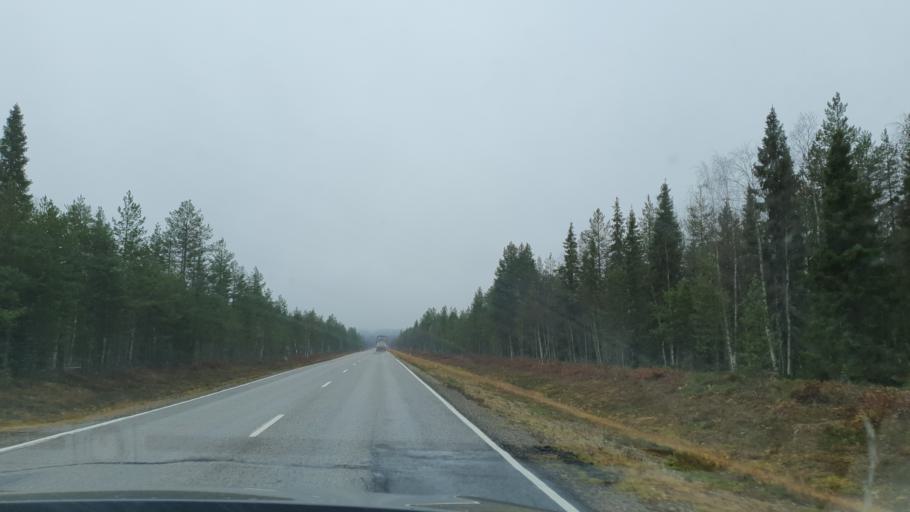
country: FI
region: Lapland
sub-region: Tunturi-Lappi
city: Kittilae
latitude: 67.4467
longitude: 24.9460
